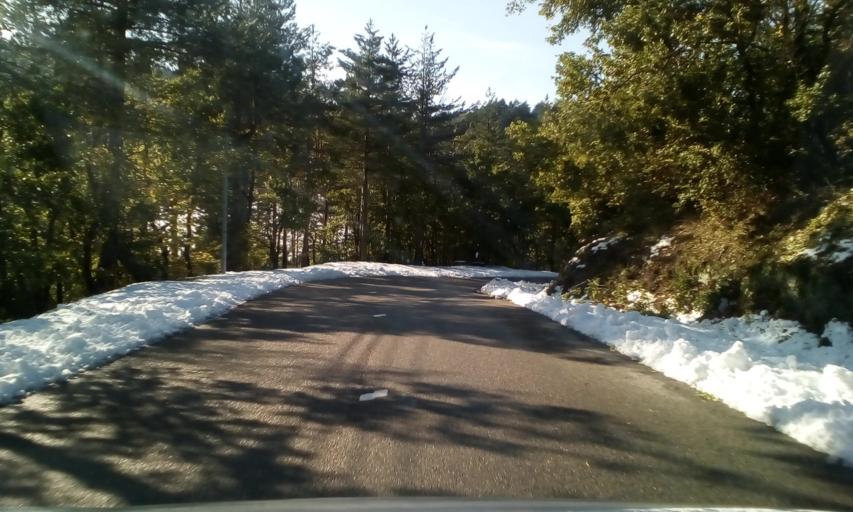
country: FR
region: Rhone-Alpes
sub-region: Departement de l'Ardeche
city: Saint-Felicien
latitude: 45.0806
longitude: 4.6080
